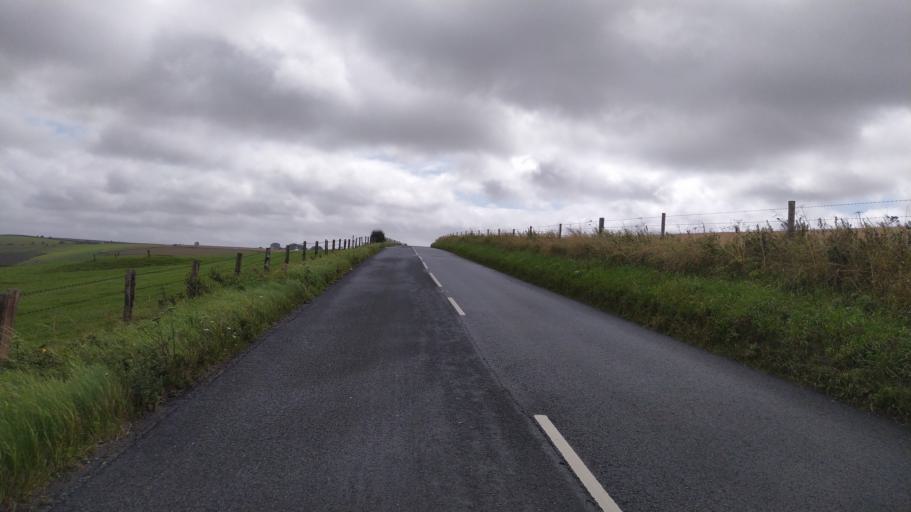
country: GB
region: England
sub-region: Dorset
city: Shaftesbury
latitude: 50.9839
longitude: -2.1383
